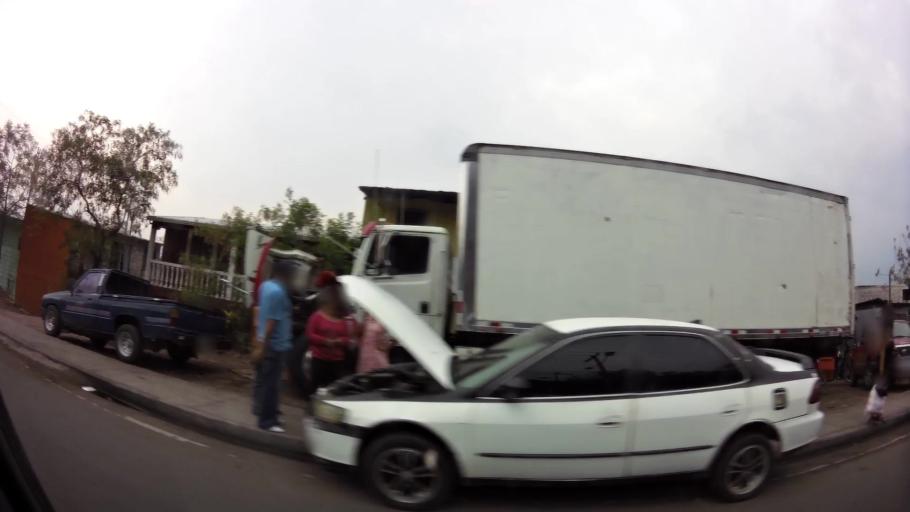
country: HN
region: Francisco Morazan
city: El Tablon
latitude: 14.0629
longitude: -87.1730
